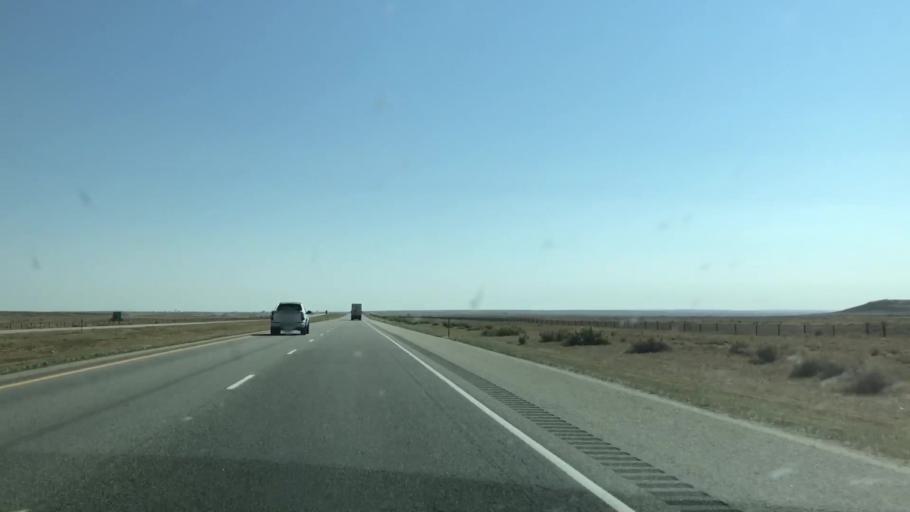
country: US
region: Wyoming
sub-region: Carbon County
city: Rawlins
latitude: 41.6592
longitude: -108.0765
